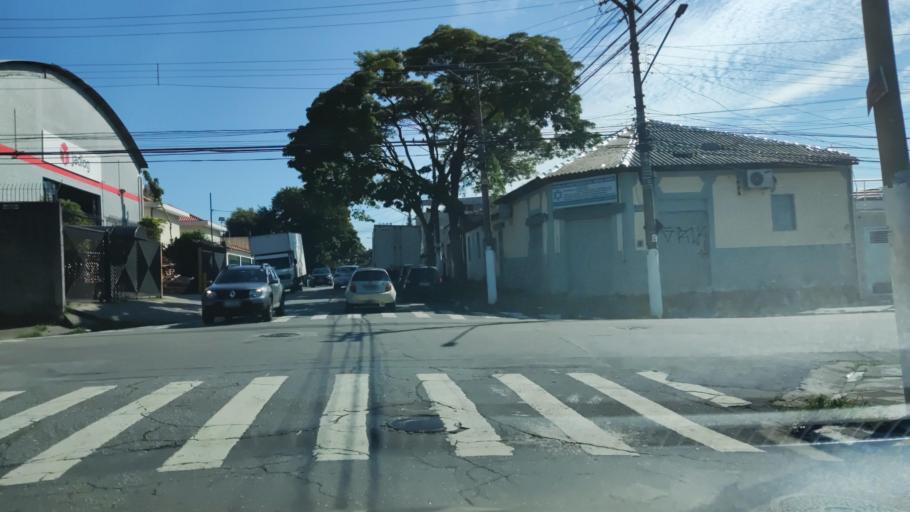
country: BR
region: Sao Paulo
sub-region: Osasco
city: Osasco
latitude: -23.5281
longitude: -46.7652
